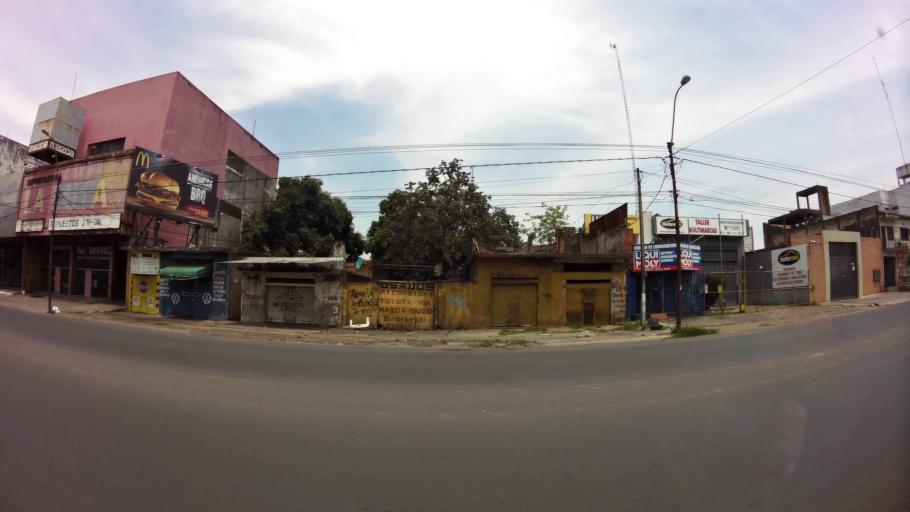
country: PY
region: Central
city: Fernando de la Mora
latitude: -25.3190
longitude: -57.5653
